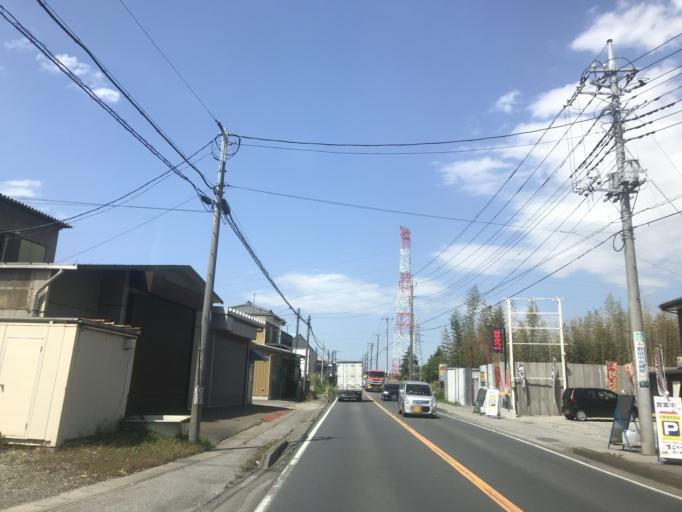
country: JP
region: Chiba
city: Noda
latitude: 35.9714
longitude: 139.8843
